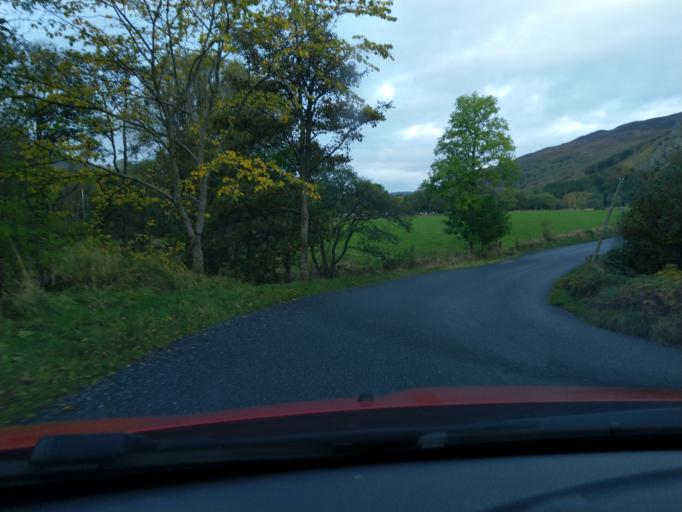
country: GB
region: Scotland
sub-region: Perth and Kinross
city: Aberfeldy
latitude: 56.6990
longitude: -4.1621
